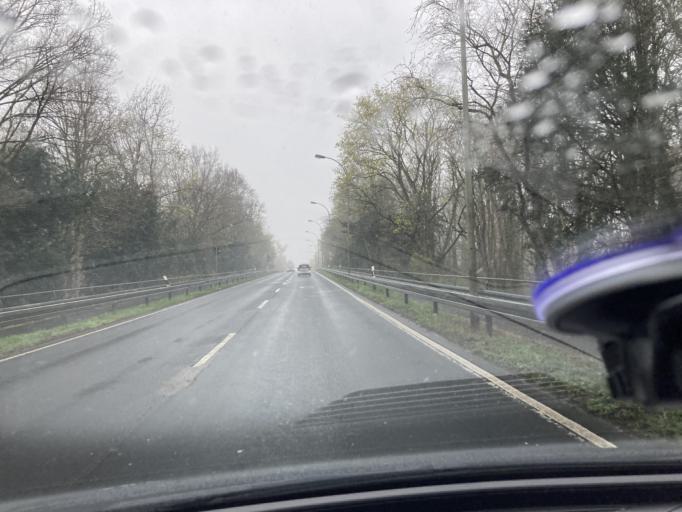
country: DE
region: Hesse
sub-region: Regierungsbezirk Darmstadt
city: Offenbach
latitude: 50.1386
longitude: 8.7605
